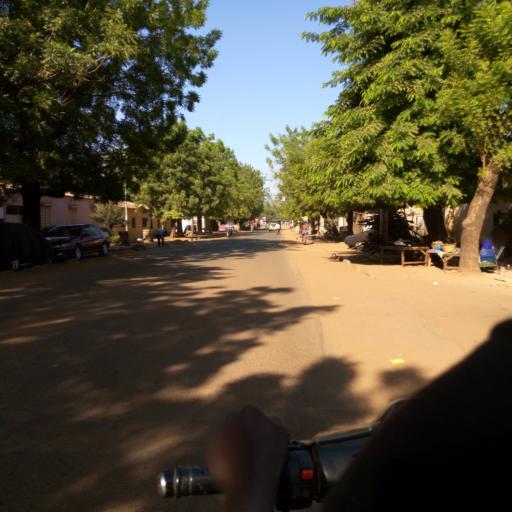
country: ML
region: Bamako
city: Bamako
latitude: 12.6559
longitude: -8.0177
